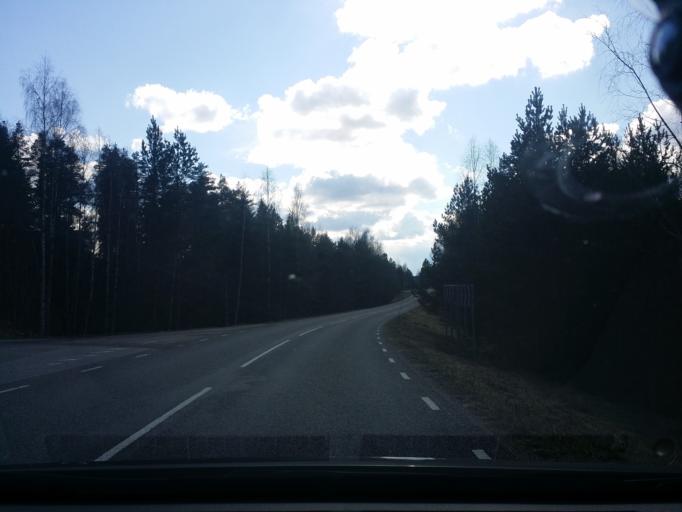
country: SE
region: Vaestmanland
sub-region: Sala Kommun
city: Sala
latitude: 59.9922
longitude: 16.4832
